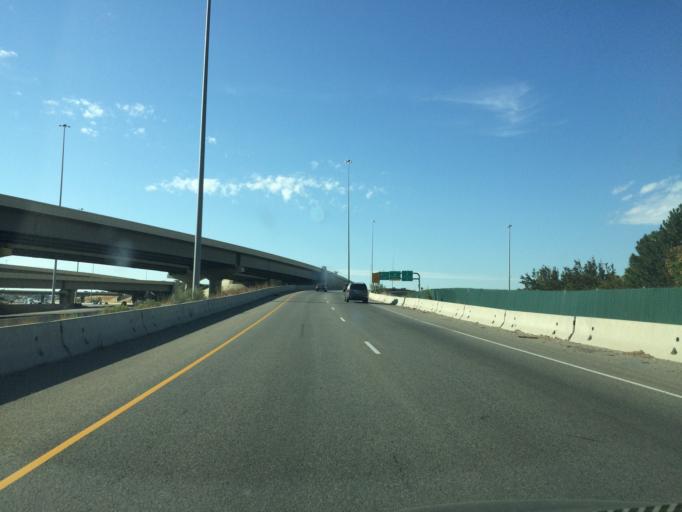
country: US
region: Utah
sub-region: Davis County
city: Farmington
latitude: 40.9861
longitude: -111.8997
